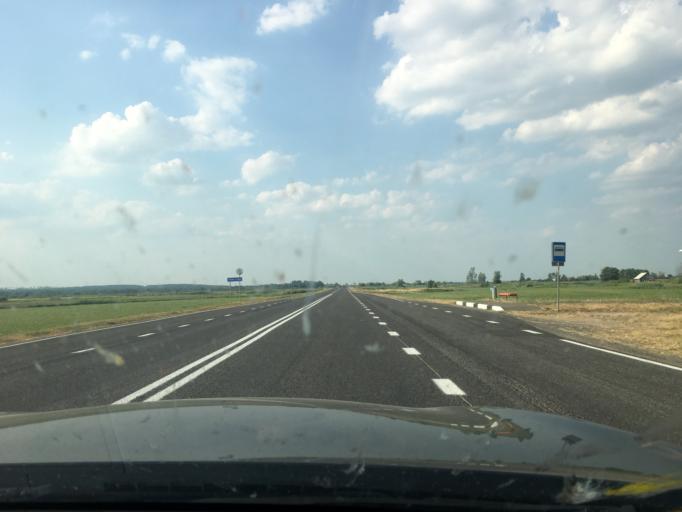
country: BY
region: Grodnenskaya
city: Indura
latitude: 53.3913
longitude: 23.9516
